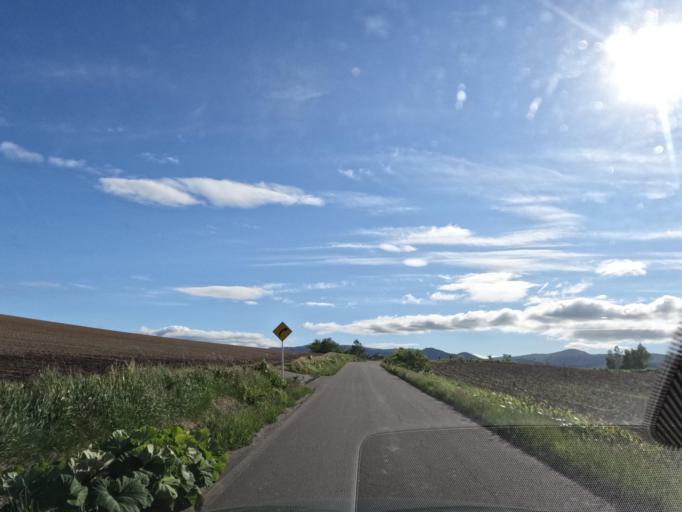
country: JP
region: Hokkaido
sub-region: Asahikawa-shi
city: Asahikawa
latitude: 43.5984
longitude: 142.4260
